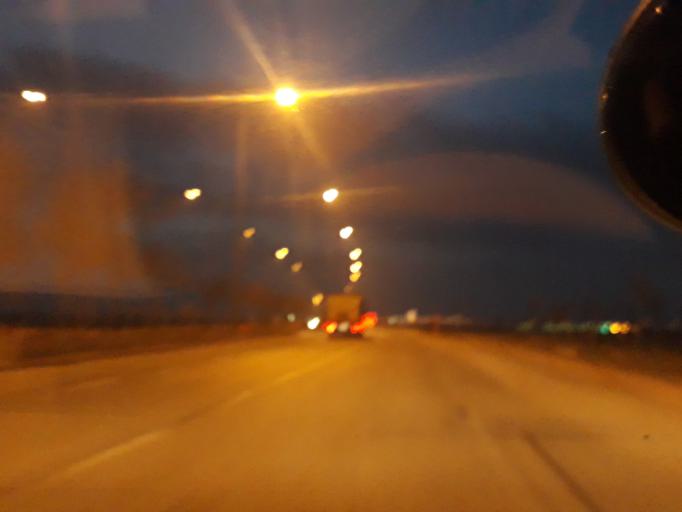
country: TR
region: Konya
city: Asagipinarbasi
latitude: 38.0051
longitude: 32.5541
